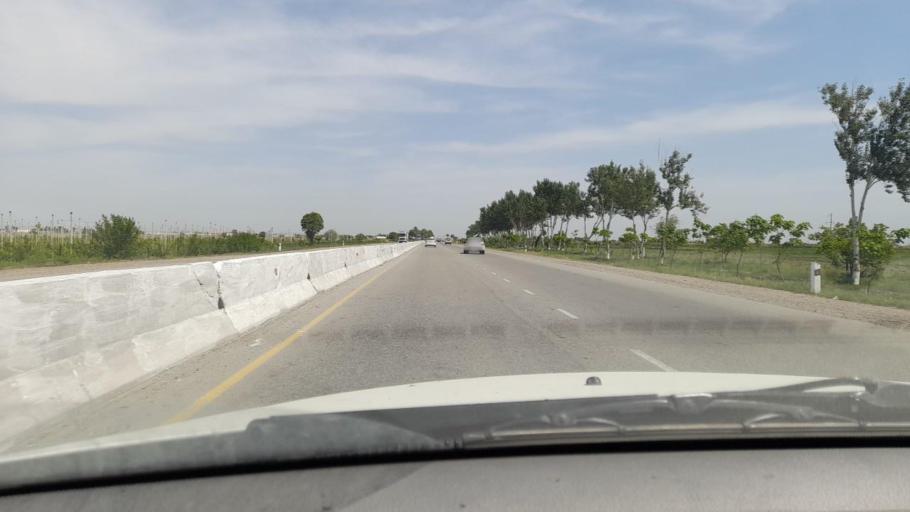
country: UZ
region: Bukhara
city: Galaosiyo
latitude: 39.8899
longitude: 64.4660
